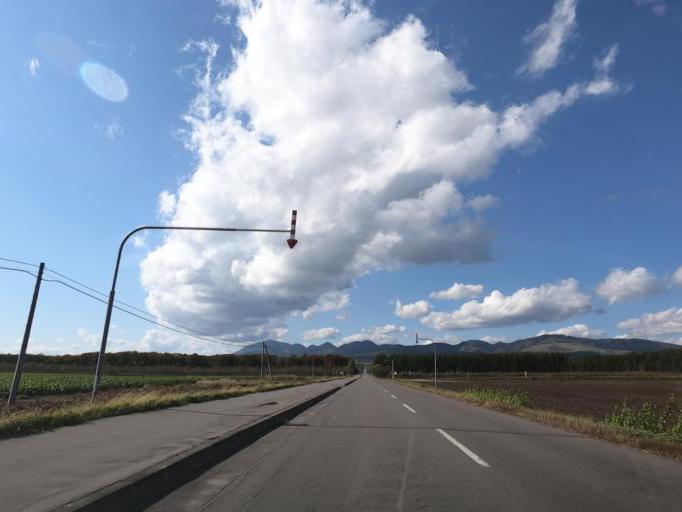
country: JP
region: Hokkaido
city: Otofuke
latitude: 43.2411
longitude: 143.2580
